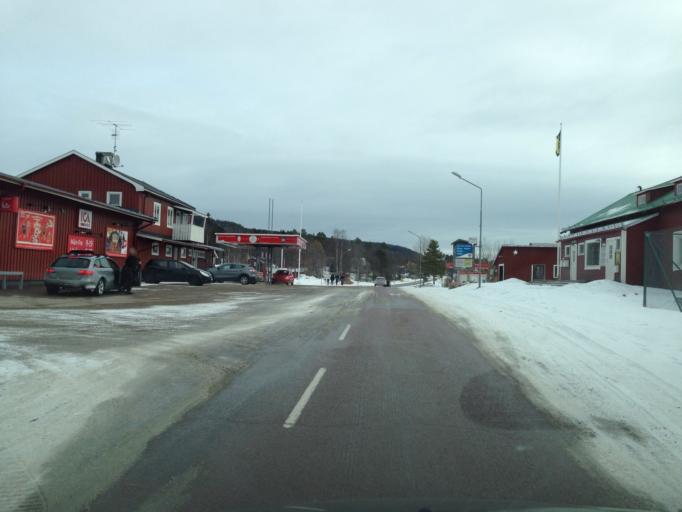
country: SE
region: Jaemtland
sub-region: Harjedalens Kommun
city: Sveg
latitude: 62.1123
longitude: 13.2716
